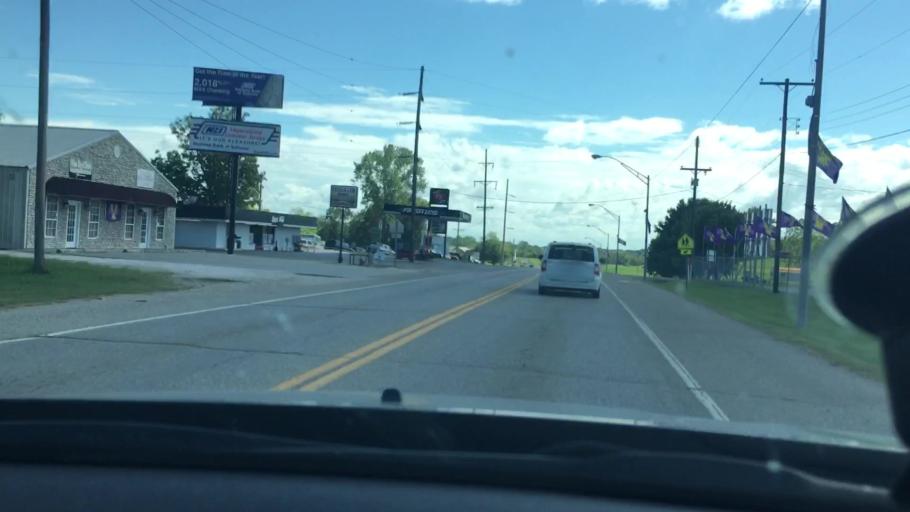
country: US
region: Oklahoma
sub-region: Sequoyah County
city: Vian
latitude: 35.4946
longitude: -94.9709
